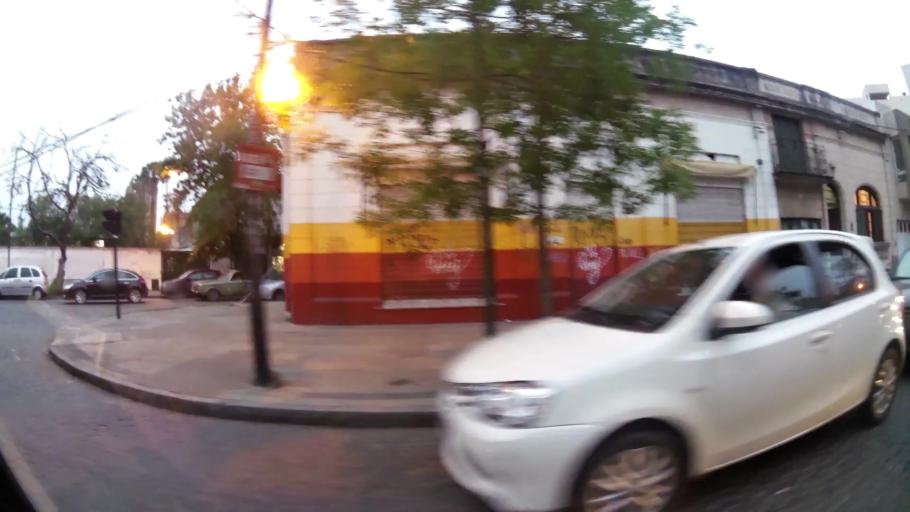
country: AR
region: Buenos Aires
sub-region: Partido de La Plata
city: La Plata
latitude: -34.9218
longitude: -57.9620
